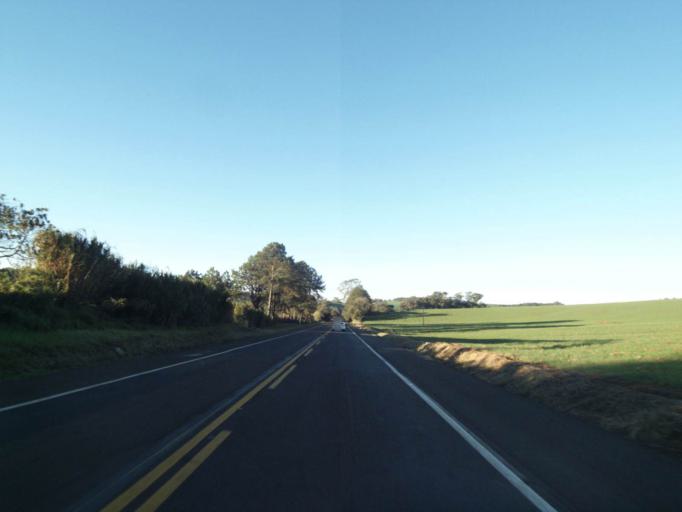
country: BR
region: Parana
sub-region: Faxinal
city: Faxinal
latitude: -23.8906
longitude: -51.1854
